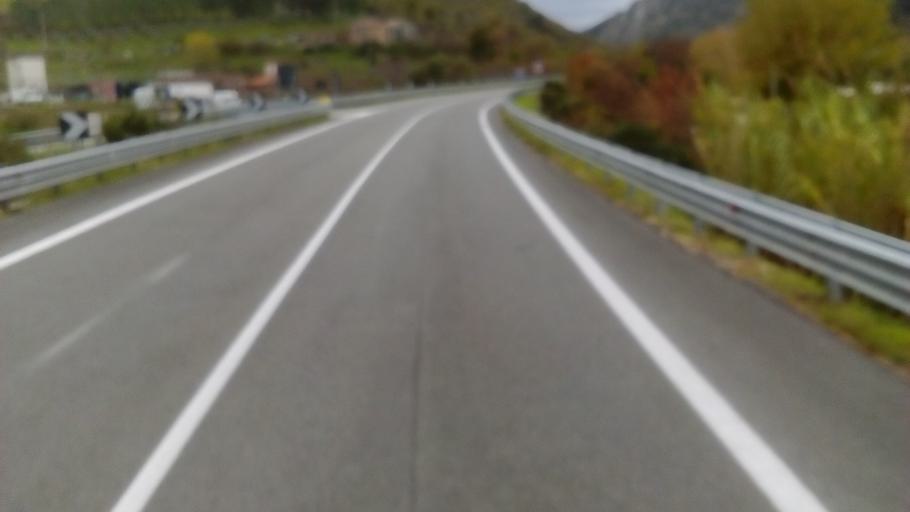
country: IT
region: Molise
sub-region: Provincia di Campobasso
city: Trivento
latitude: 41.7984
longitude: 14.5600
